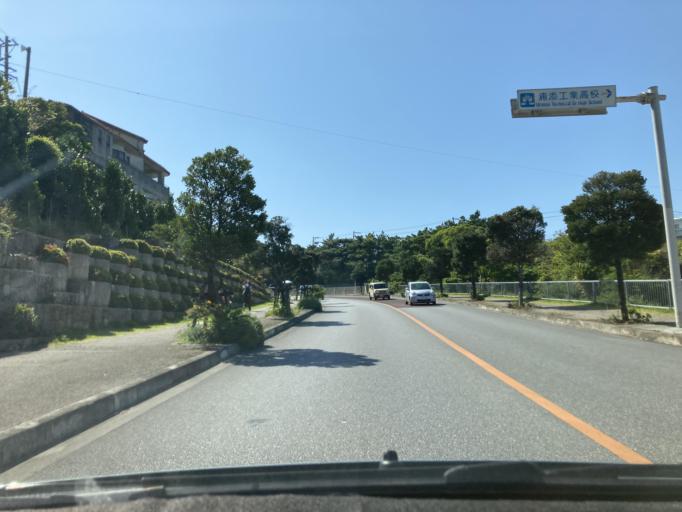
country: JP
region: Okinawa
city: Ginowan
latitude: 26.2433
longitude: 127.7258
